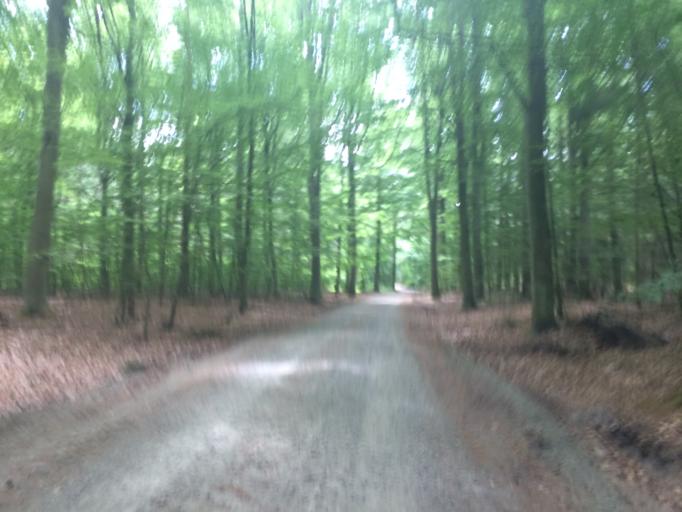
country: DK
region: Capital Region
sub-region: Bornholm Kommune
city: Ronne
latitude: 55.1342
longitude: 14.7158
